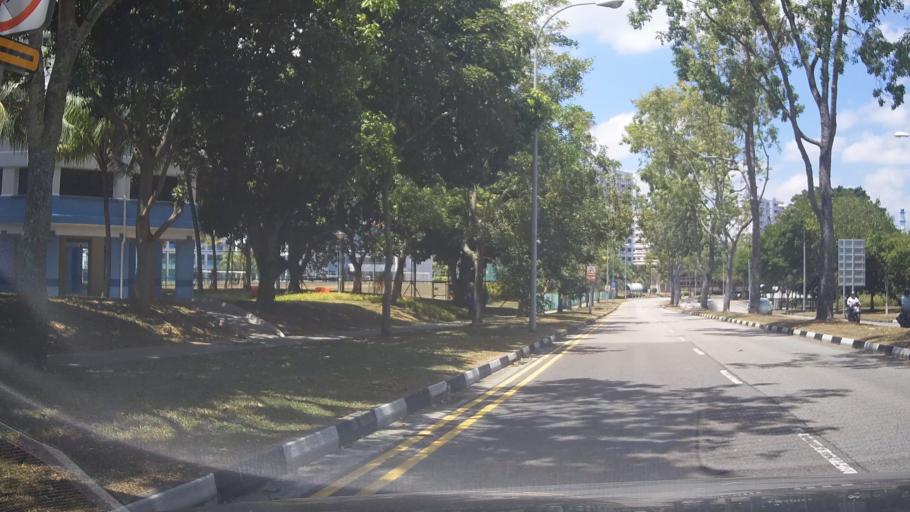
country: MY
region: Johor
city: Kampung Pasir Gudang Baru
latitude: 1.3684
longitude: 103.9647
